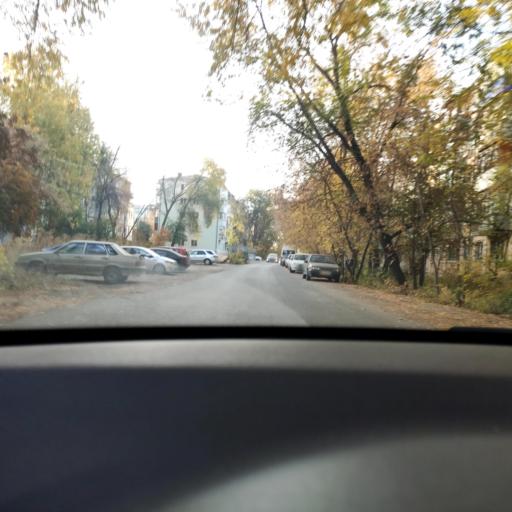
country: RU
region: Samara
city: Samara
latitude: 53.2142
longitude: 50.1979
